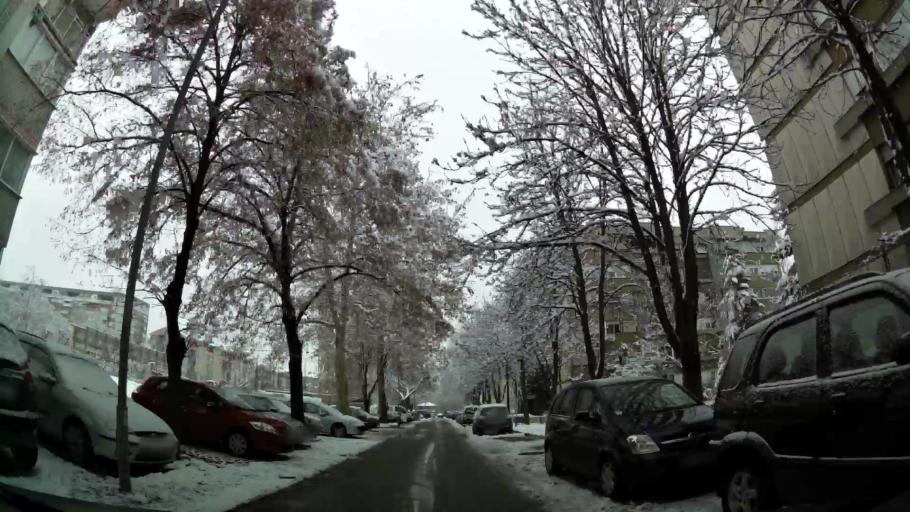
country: RS
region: Central Serbia
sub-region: Belgrade
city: Zemun
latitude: 44.8320
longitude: 20.4161
